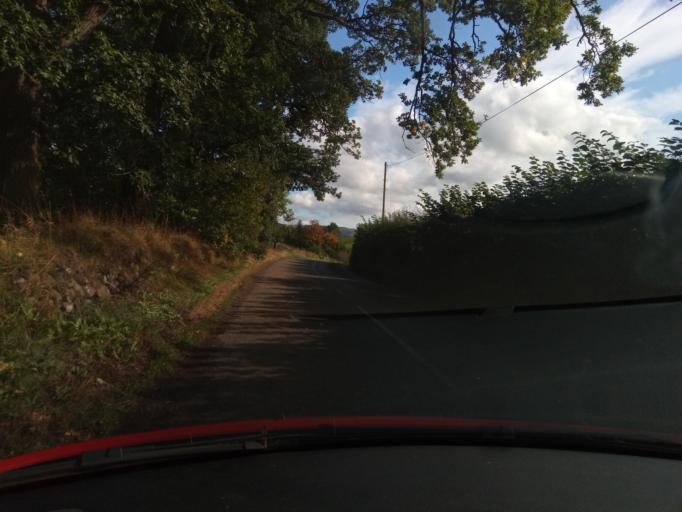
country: GB
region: Scotland
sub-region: The Scottish Borders
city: Kelso
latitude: 55.5566
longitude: -2.3261
